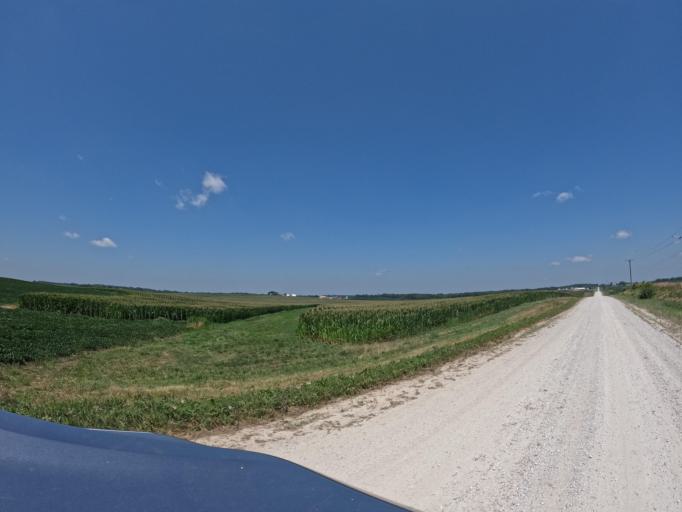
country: US
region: Iowa
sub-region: Keokuk County
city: Sigourney
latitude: 41.2831
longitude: -92.2190
